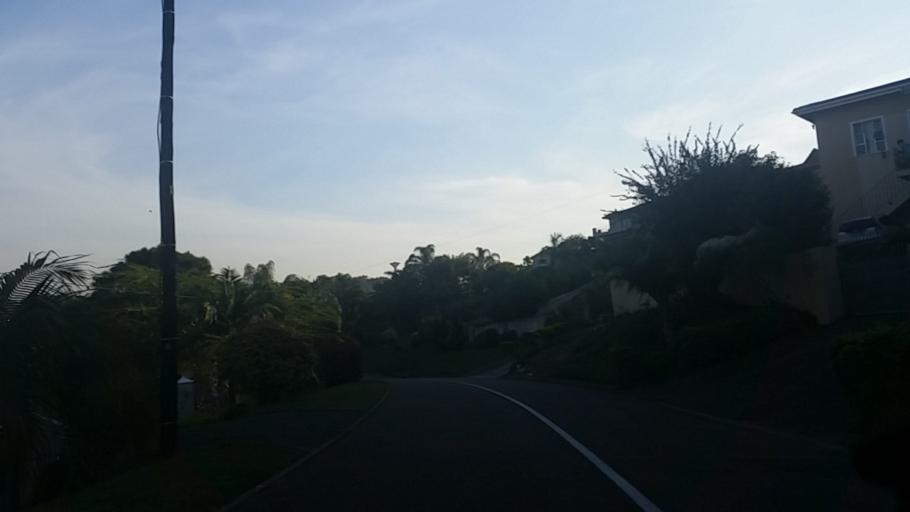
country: ZA
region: KwaZulu-Natal
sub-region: eThekwini Metropolitan Municipality
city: Berea
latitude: -29.8505
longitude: 30.9229
